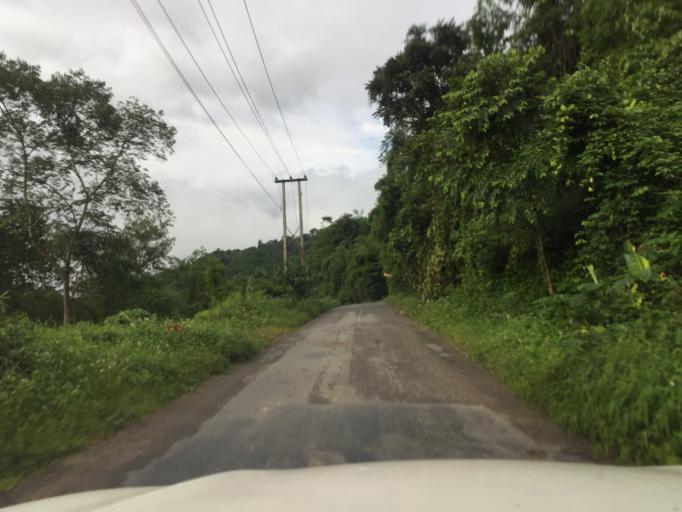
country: LA
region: Oudomxai
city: Muang La
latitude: 21.0698
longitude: 102.2417
